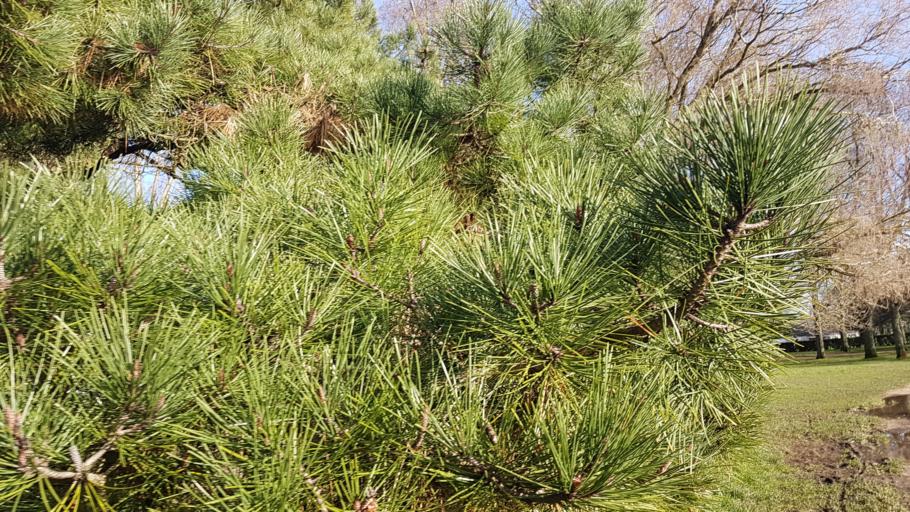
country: FR
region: Pays de la Loire
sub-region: Departement de la Loire-Atlantique
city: Saint-Nazaire
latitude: 47.2737
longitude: -2.2252
